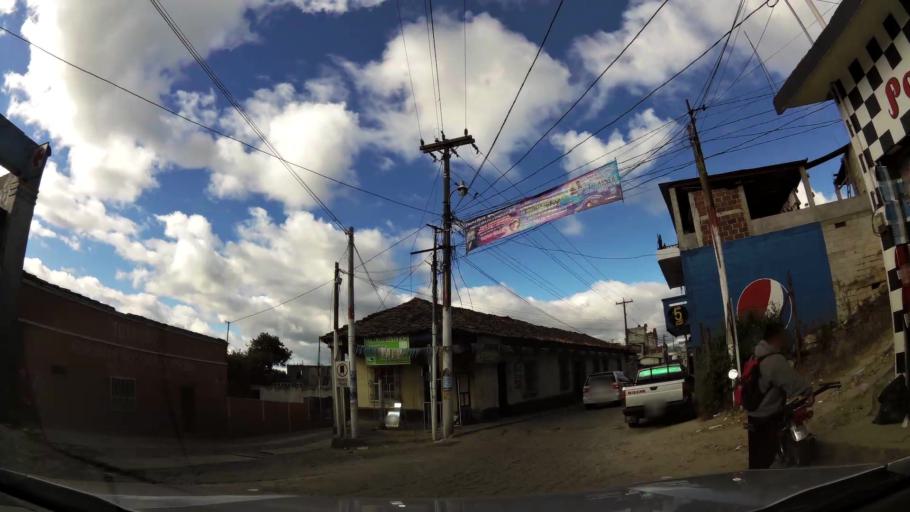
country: GT
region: Quiche
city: Chichicastenango
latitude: 14.9381
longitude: -91.1109
